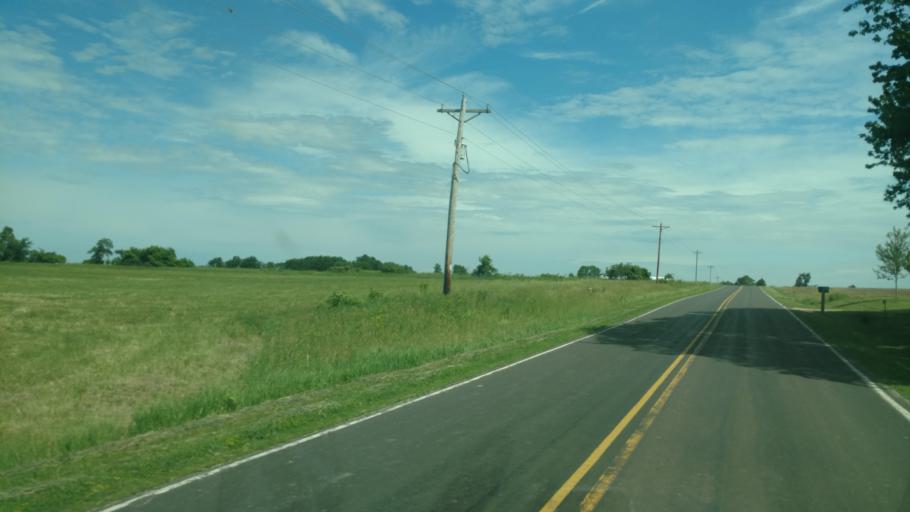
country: US
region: Wisconsin
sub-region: Vernon County
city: Hillsboro
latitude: 43.7077
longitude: -90.4527
